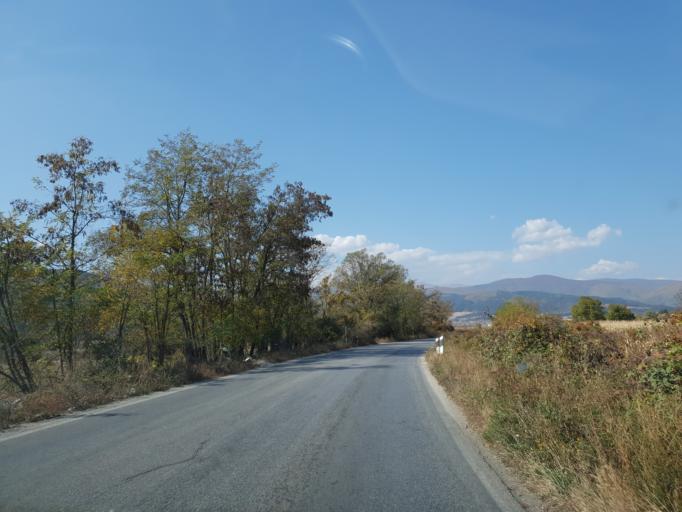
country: MK
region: Kicevo
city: Kicevo
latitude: 41.4785
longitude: 20.9832
